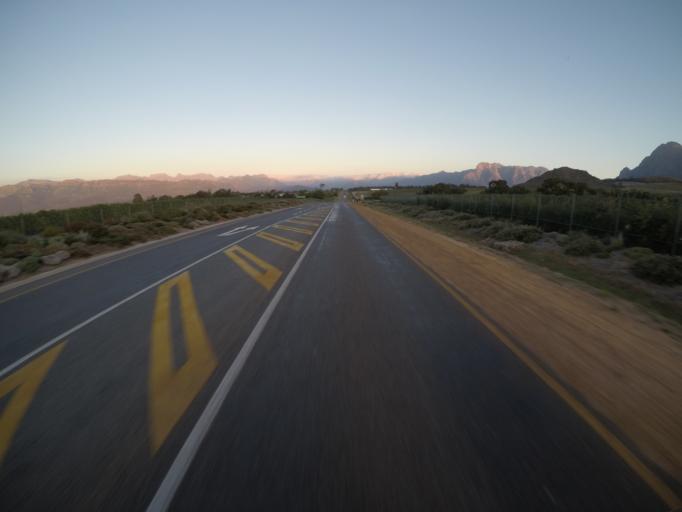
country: ZA
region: Western Cape
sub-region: Cape Winelands District Municipality
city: Paarl
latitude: -33.8219
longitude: 18.9292
